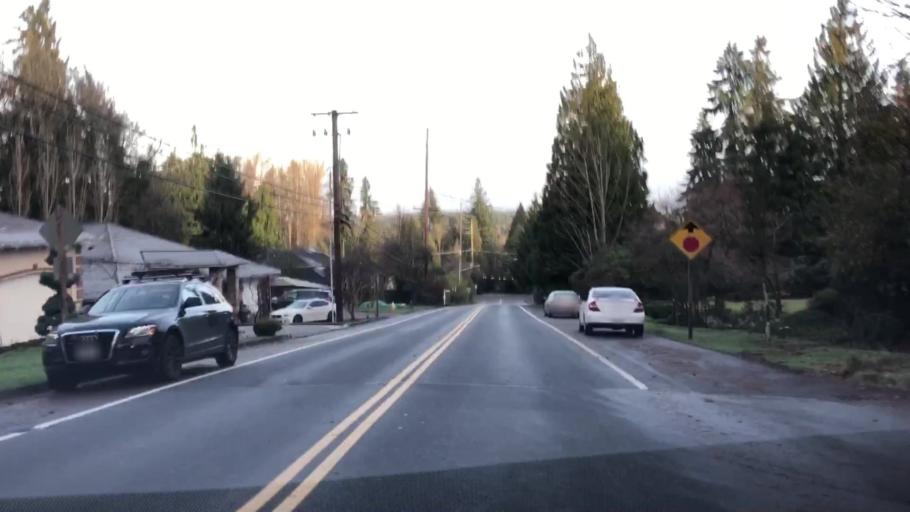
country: US
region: Washington
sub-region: King County
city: West Lake Sammamish
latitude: 47.5706
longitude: -122.1216
